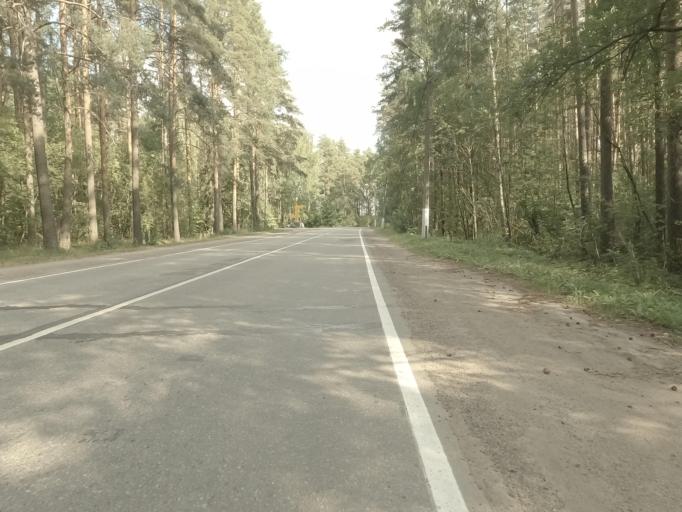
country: RU
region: Leningrad
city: Kamennogorsk
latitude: 60.9439
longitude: 29.1483
